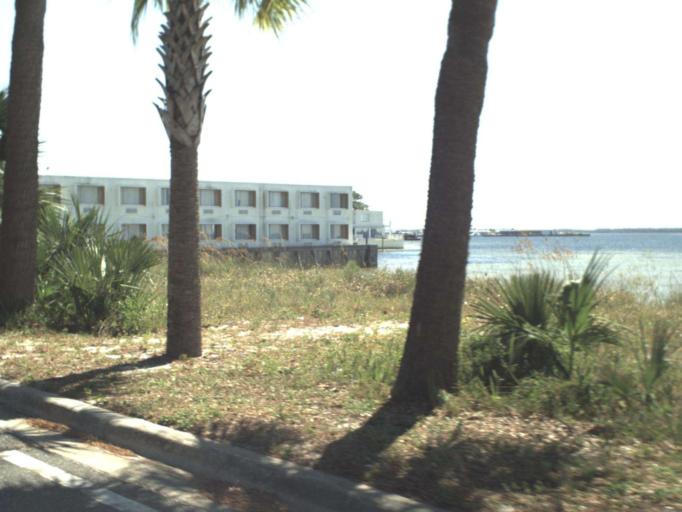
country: US
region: Florida
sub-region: Bay County
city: Panama City
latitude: 30.1599
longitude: -85.6706
